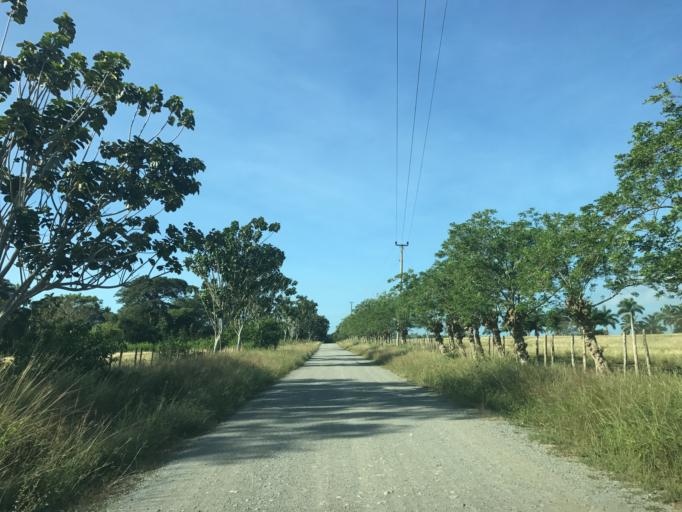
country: CU
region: Camaguey
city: Florida
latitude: 21.4840
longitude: -78.1739
